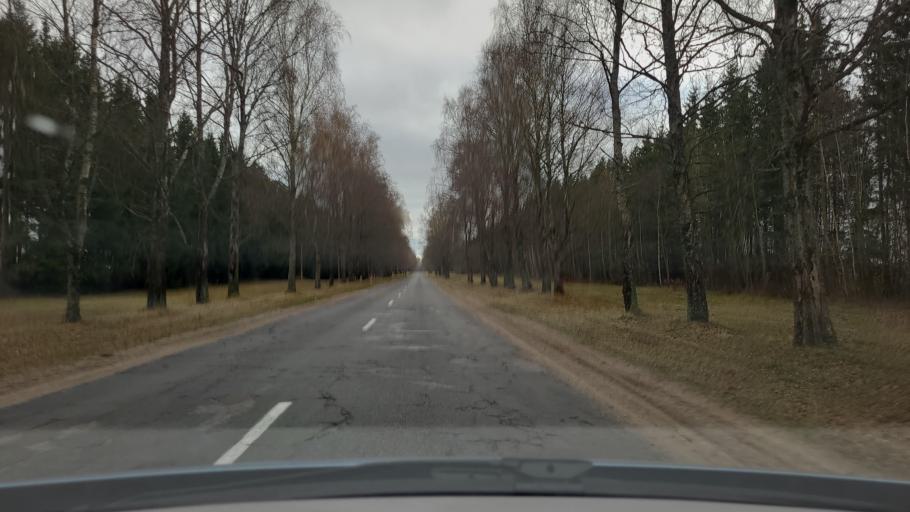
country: BY
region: Minsk
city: Khalopyenichy
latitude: 54.4924
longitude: 28.9547
